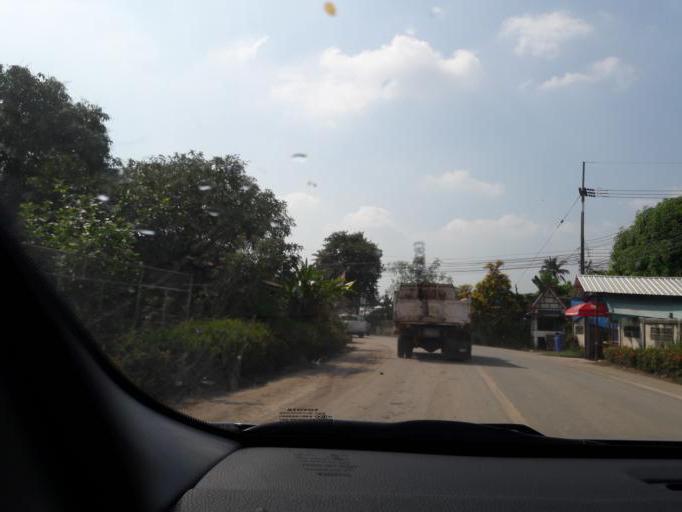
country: TH
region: Ang Thong
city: Ang Thong
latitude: 14.5700
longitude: 100.4143
